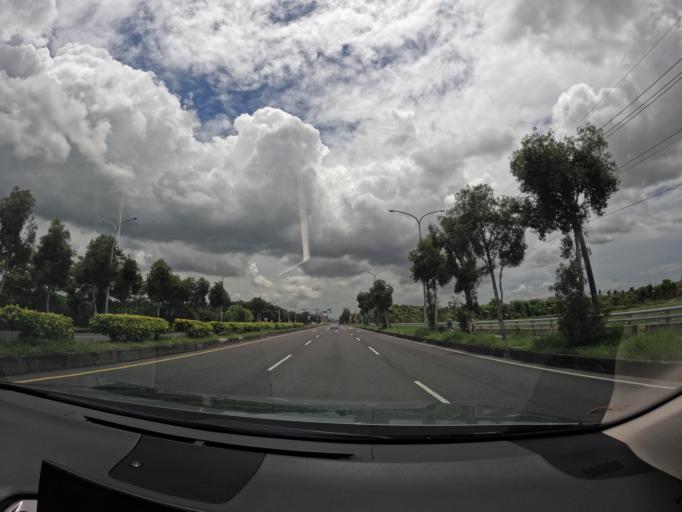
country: TW
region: Kaohsiung
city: Kaohsiung
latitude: 22.7722
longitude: 120.3029
